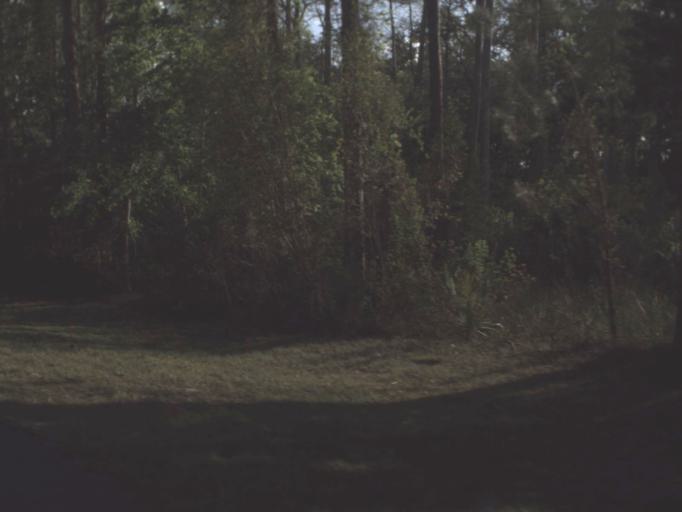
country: US
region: Florida
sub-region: Flagler County
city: Bunnell
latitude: 29.3669
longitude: -81.3117
